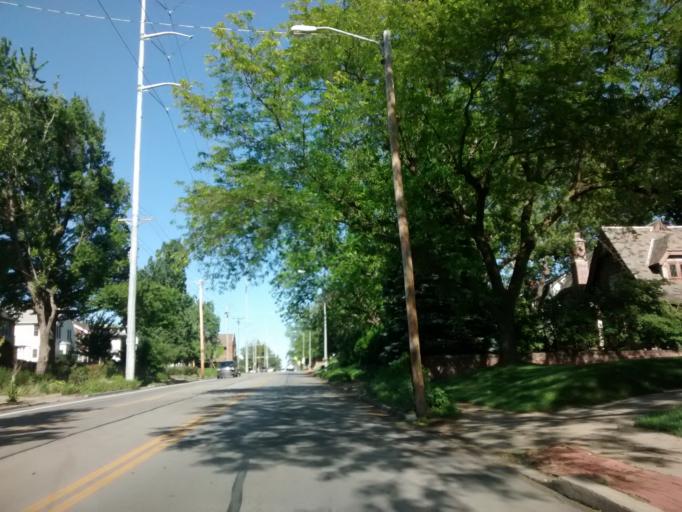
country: US
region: Nebraska
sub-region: Douglas County
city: Ralston
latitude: 41.2524
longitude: -96.0013
